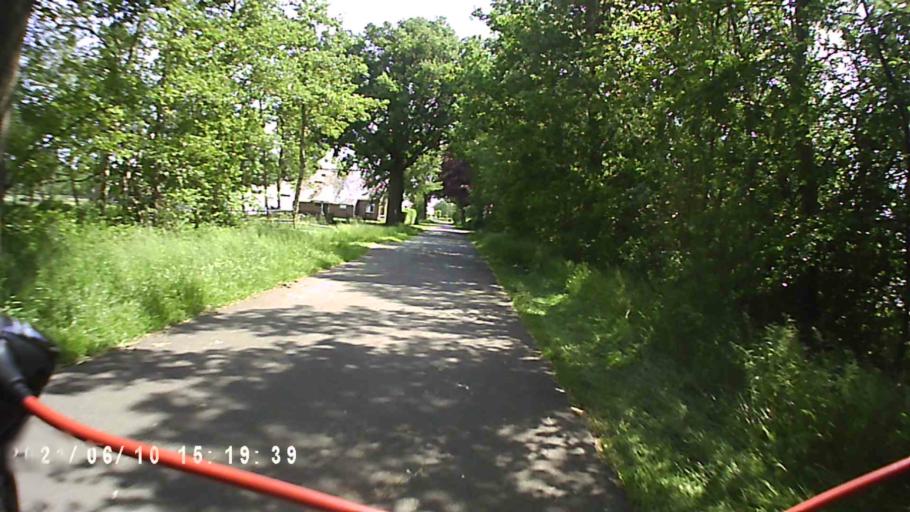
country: NL
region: Friesland
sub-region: Gemeente Achtkarspelen
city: Surhuisterveen
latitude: 53.1943
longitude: 6.1730
